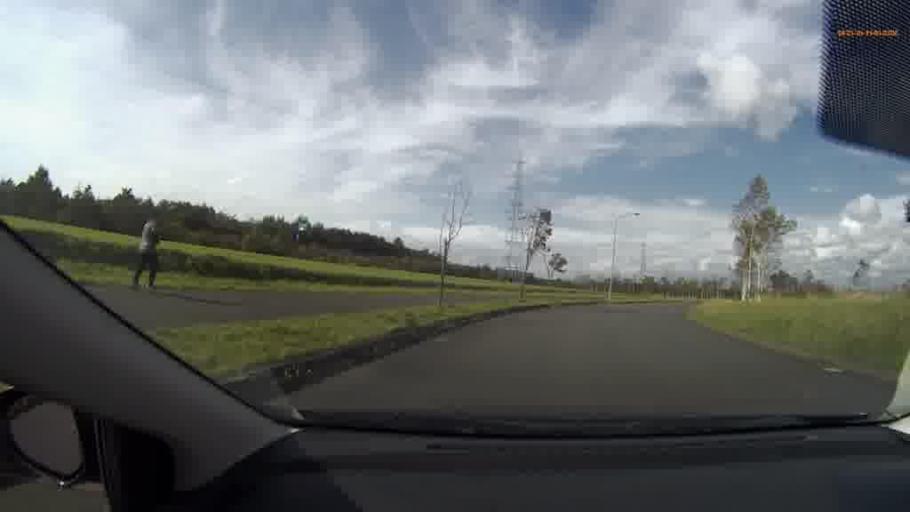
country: JP
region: Hokkaido
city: Kushiro
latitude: 43.0292
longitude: 144.4062
